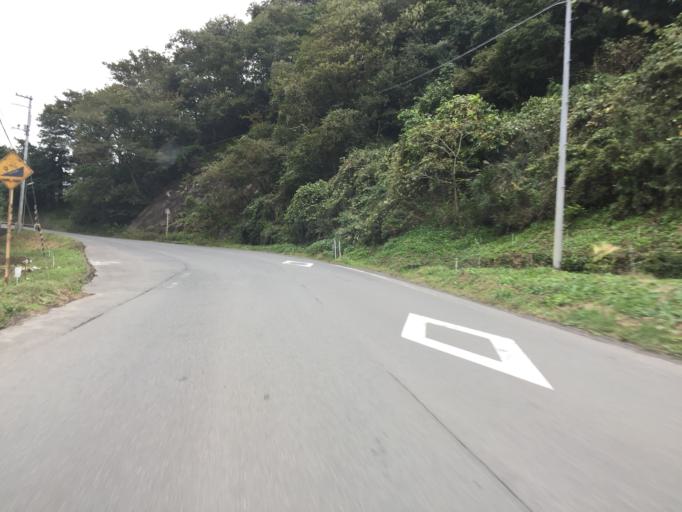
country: JP
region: Fukushima
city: Yanagawamachi-saiwaicho
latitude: 37.8793
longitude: 140.6670
